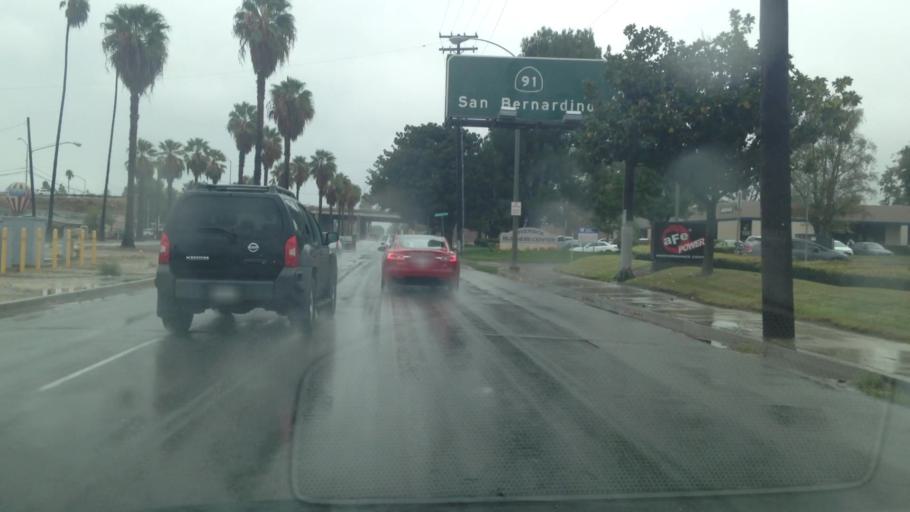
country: US
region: California
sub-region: Riverside County
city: Home Gardens
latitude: 33.8954
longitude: -117.4903
